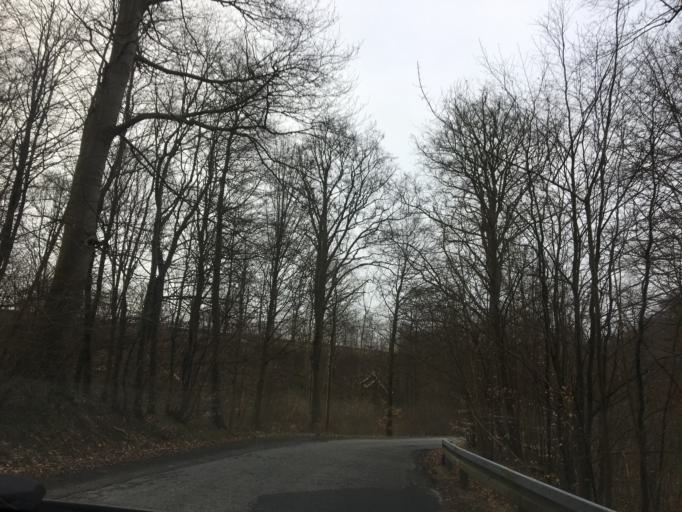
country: DK
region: South Denmark
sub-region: Vejle Kommune
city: Brejning
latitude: 55.7202
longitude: 9.6332
